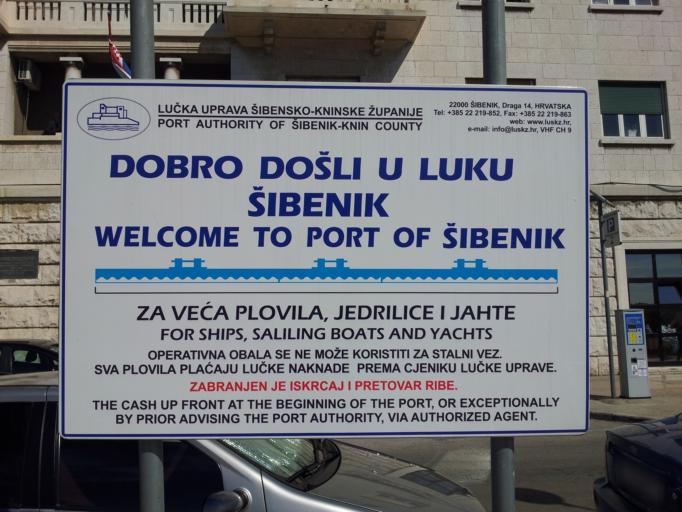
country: HR
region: Sibensko-Kniniska
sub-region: Grad Sibenik
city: Sibenik
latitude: 43.7324
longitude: 15.8923
